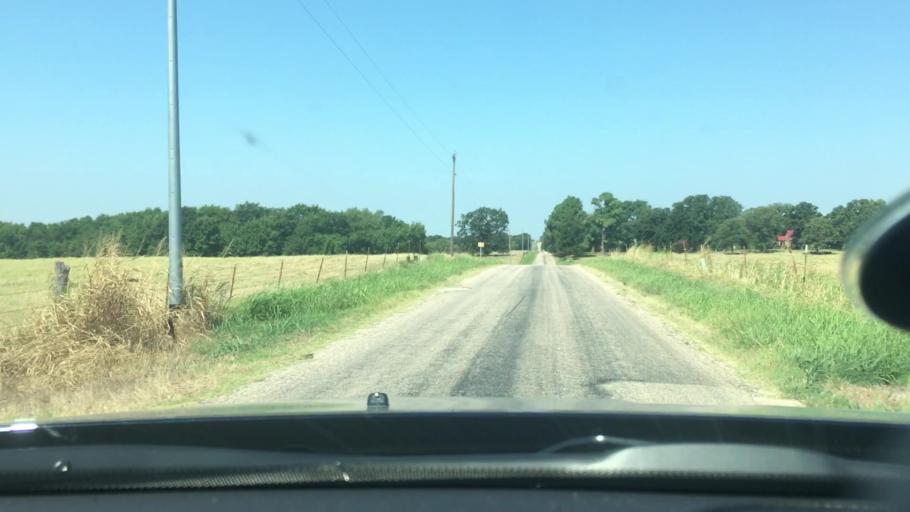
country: US
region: Oklahoma
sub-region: Johnston County
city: Tishomingo
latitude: 34.3176
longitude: -96.6408
